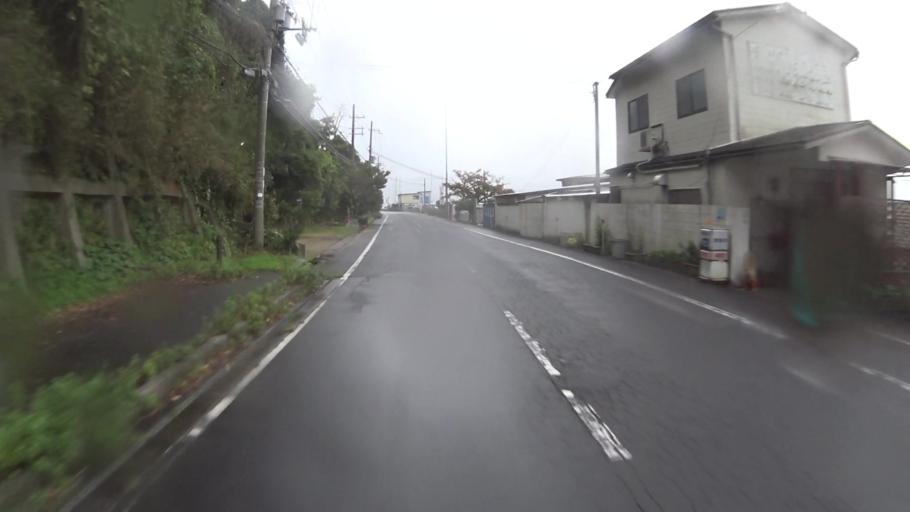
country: JP
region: Kyoto
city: Miyazu
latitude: 35.5606
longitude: 135.2051
